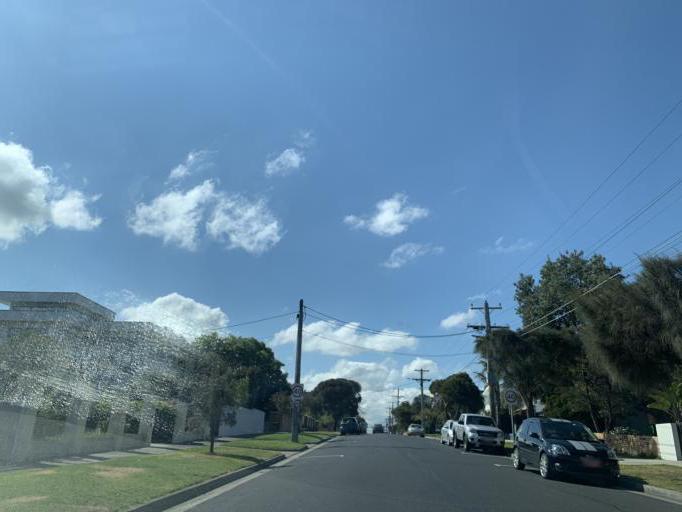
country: AU
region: Victoria
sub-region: Kingston
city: Parkdale
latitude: -37.9973
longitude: 145.0761
